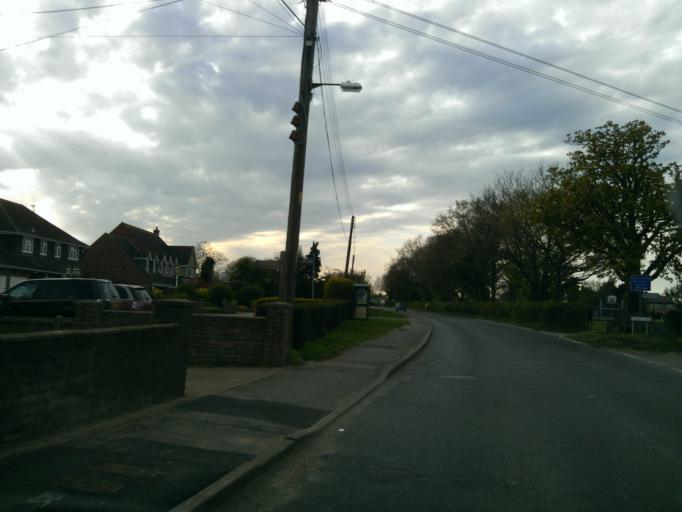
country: GB
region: England
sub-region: Essex
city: Great Bentley
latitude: 51.8391
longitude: 1.0421
